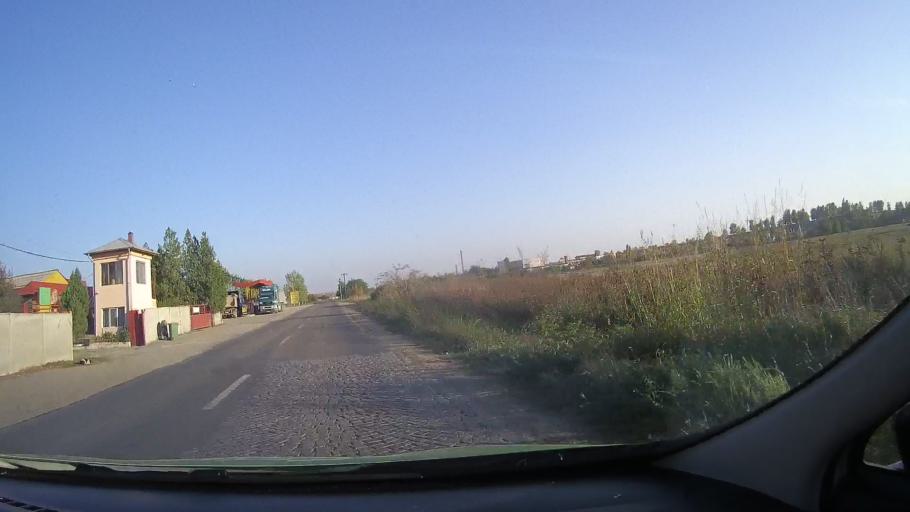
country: RO
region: Bihor
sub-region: Comuna Bors
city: Santion
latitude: 47.1048
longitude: 21.8732
